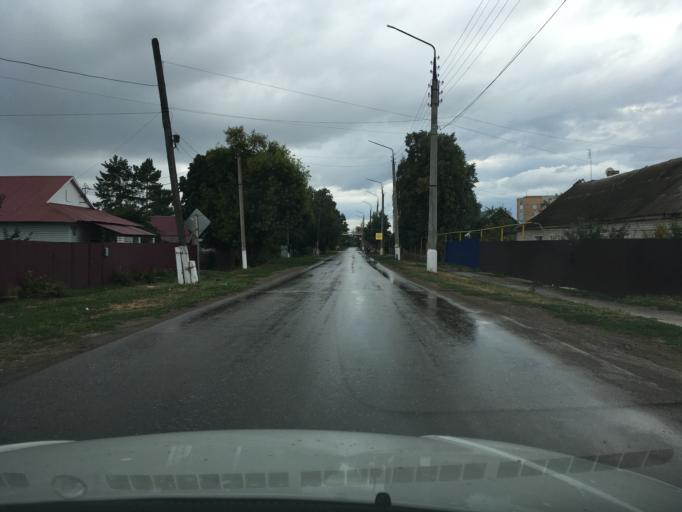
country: RU
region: Samara
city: Bezenchuk
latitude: 52.9826
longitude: 49.4394
